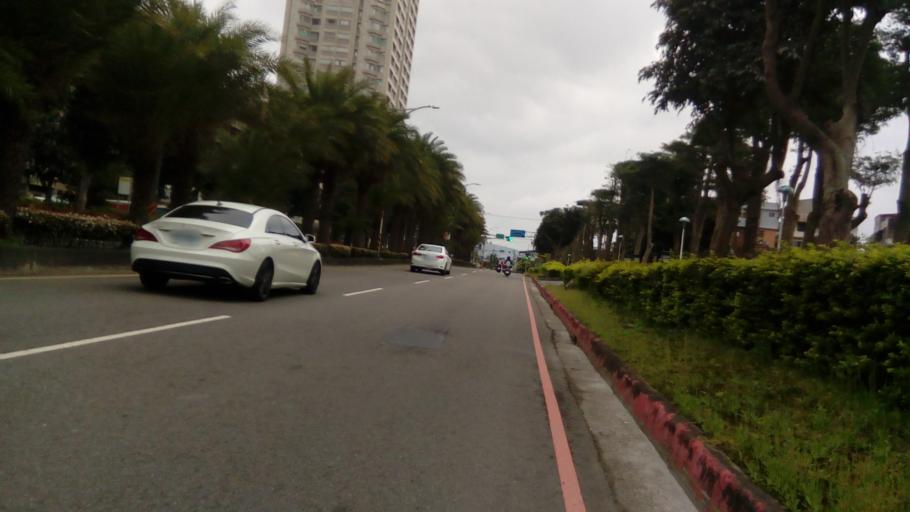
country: TW
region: Taipei
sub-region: Taipei
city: Banqiao
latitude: 25.1785
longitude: 121.4229
